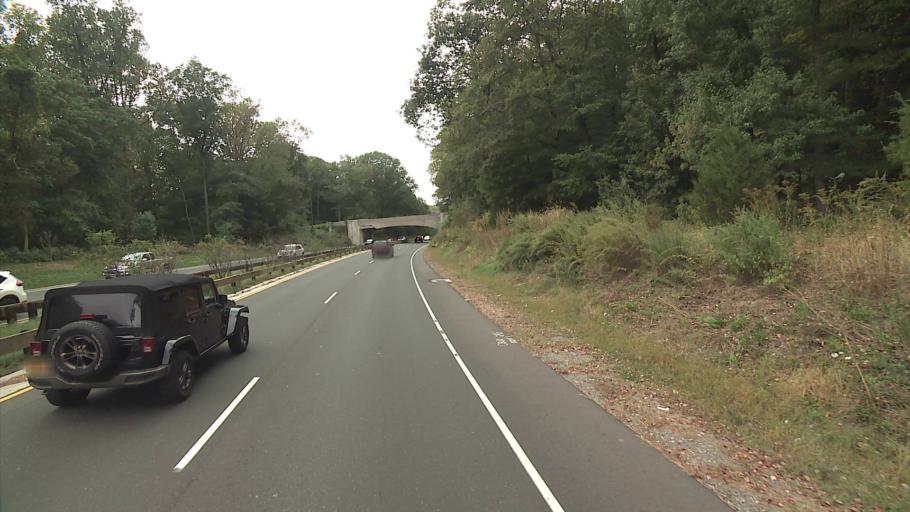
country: US
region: Connecticut
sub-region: Fairfield County
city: New Canaan
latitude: 41.1166
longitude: -73.4923
